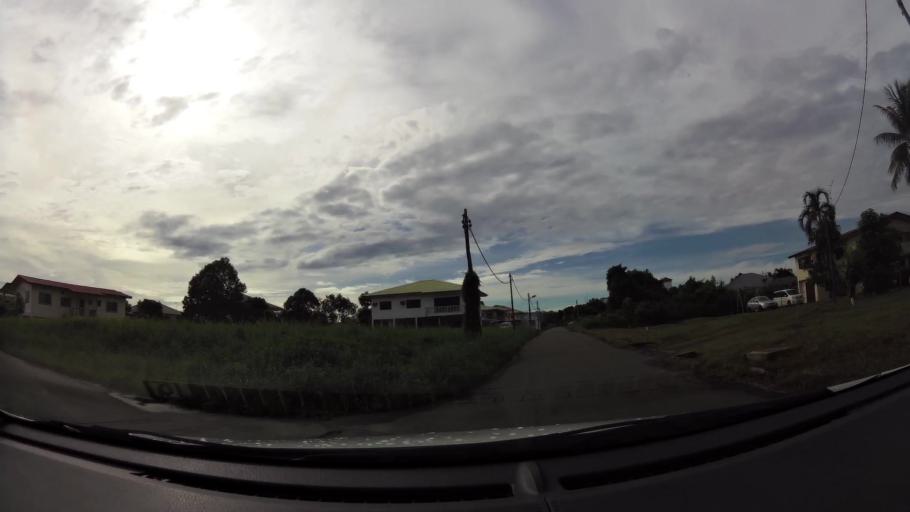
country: BN
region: Belait
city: Seria
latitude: 4.6142
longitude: 114.3603
